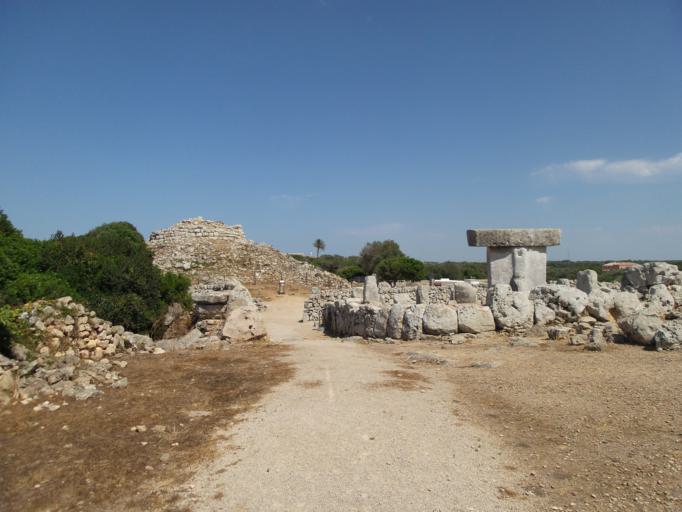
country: ES
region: Balearic Islands
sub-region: Illes Balears
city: Alaior
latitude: 39.9126
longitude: 4.1631
